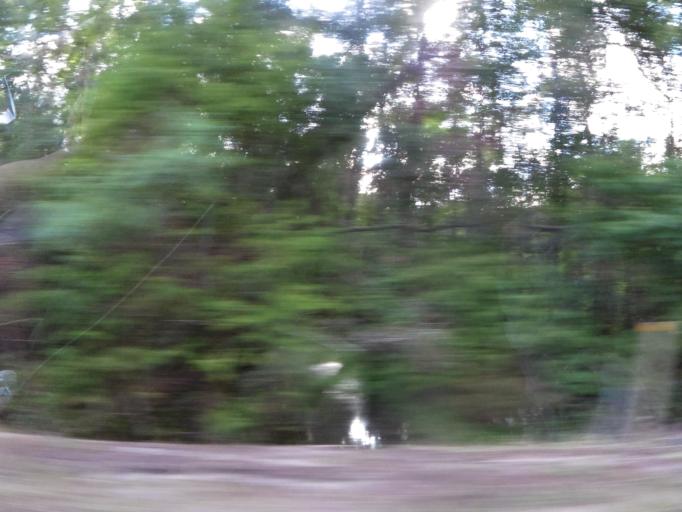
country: US
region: Georgia
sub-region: Liberty County
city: Midway
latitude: 31.6911
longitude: -81.4094
